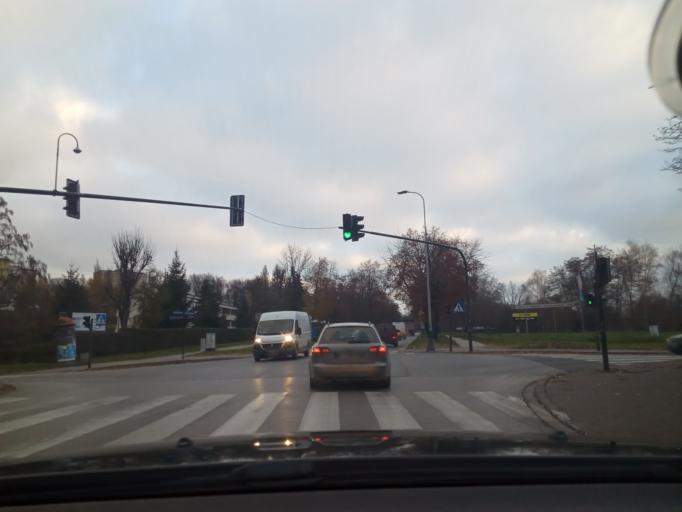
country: PL
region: Lesser Poland Voivodeship
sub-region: Powiat wielicki
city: Kokotow
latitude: 50.0908
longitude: 20.0576
